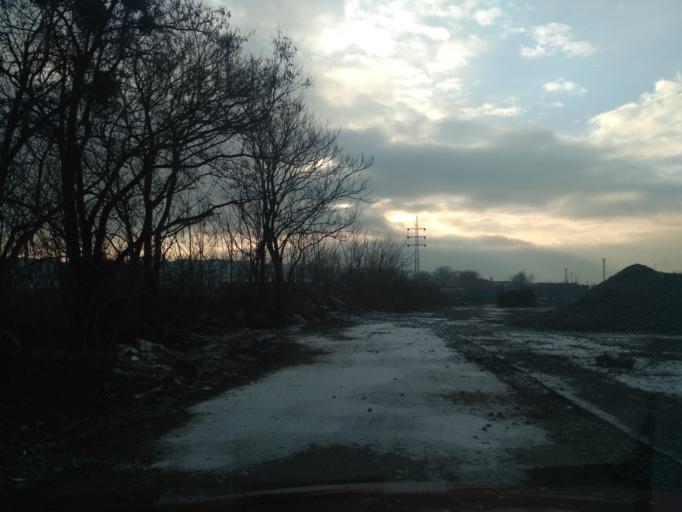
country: SK
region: Kosicky
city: Kosice
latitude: 48.7329
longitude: 21.2644
